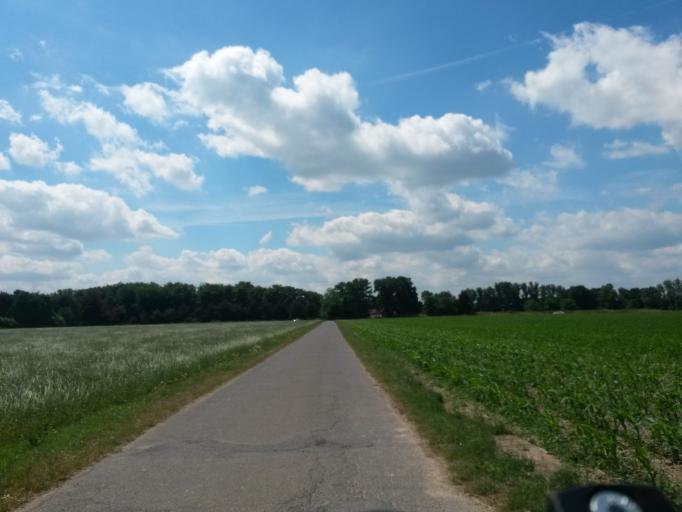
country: DE
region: North Rhine-Westphalia
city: Kempen
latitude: 51.3575
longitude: 6.4498
